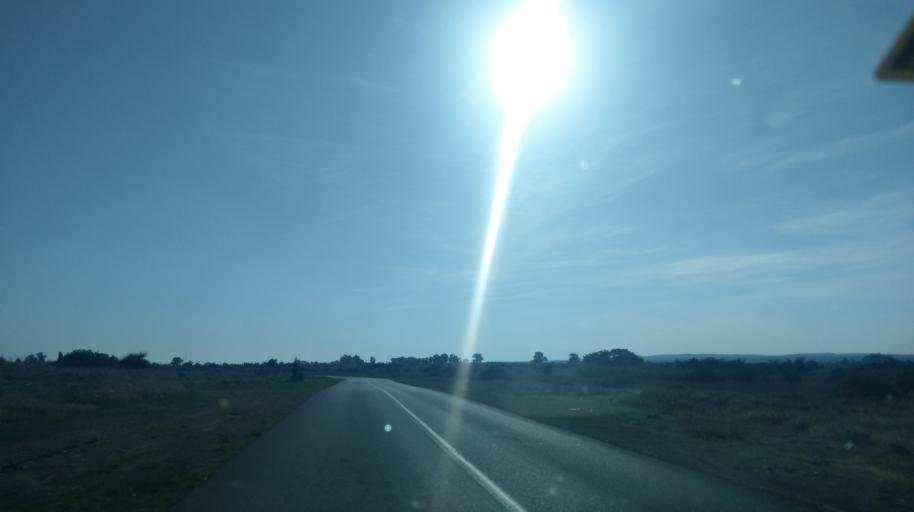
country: CY
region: Larnaka
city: Pergamos
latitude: 35.0869
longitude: 33.7218
